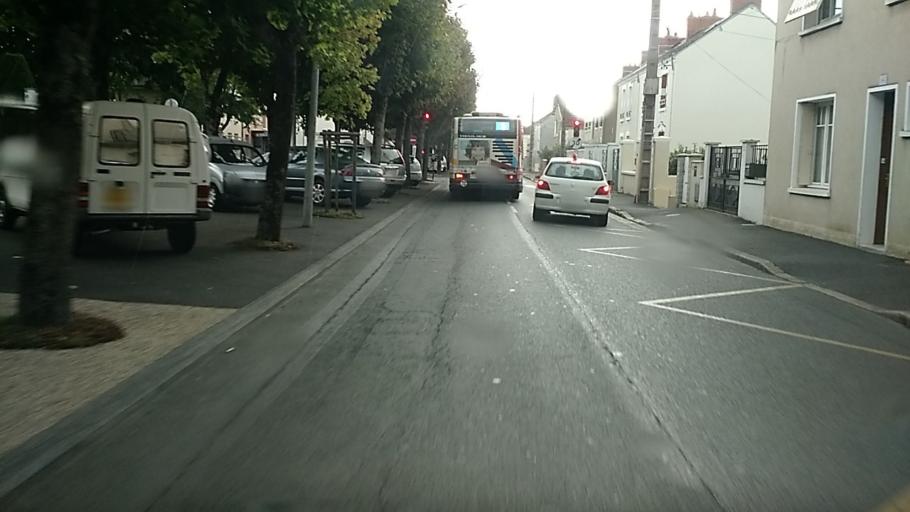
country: FR
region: Centre
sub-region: Departement de l'Indre
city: Chateauroux
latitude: 46.8163
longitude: 1.7091
